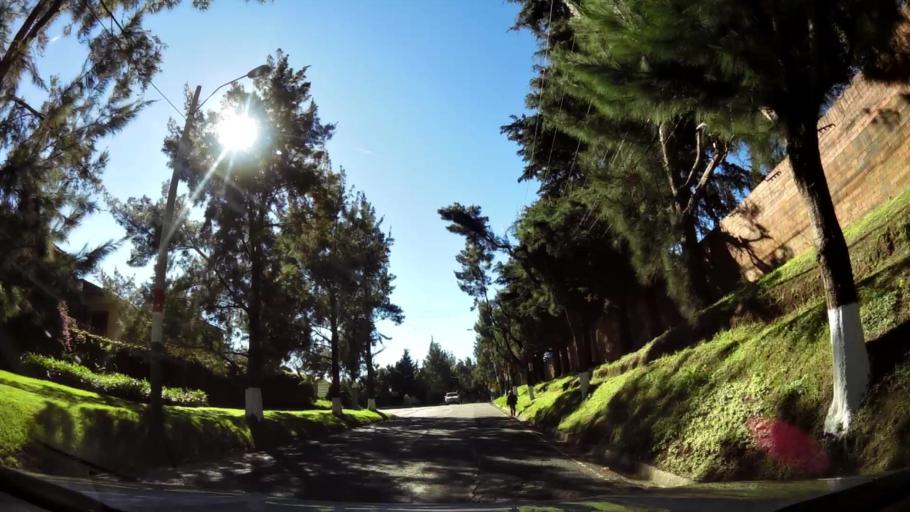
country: GT
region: Guatemala
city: Fraijanes
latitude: 14.5119
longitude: -90.4653
